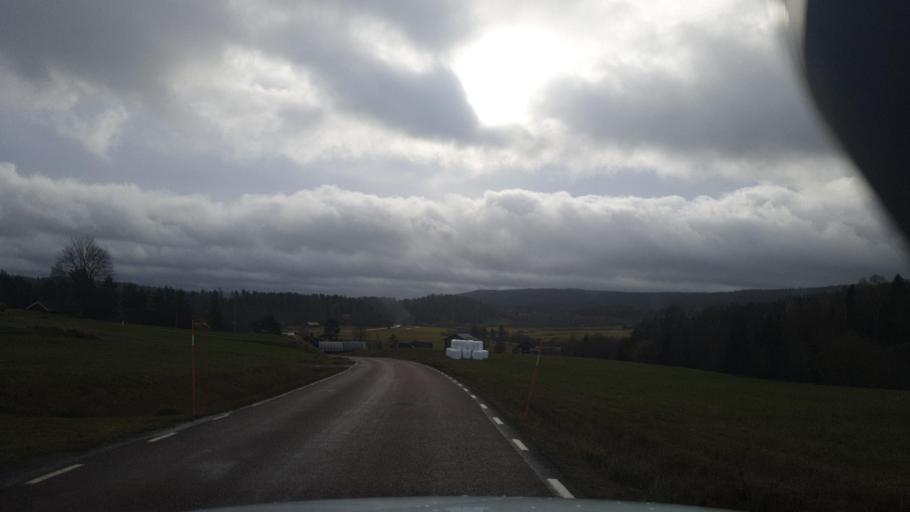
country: NO
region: Ostfold
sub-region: Romskog
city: Romskog
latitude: 59.7130
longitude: 12.0699
